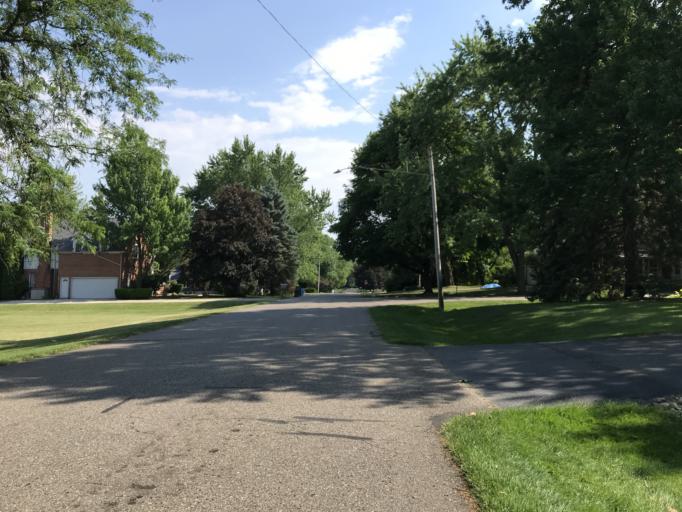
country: US
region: Michigan
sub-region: Oakland County
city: Farmington
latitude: 42.4670
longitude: -83.3891
